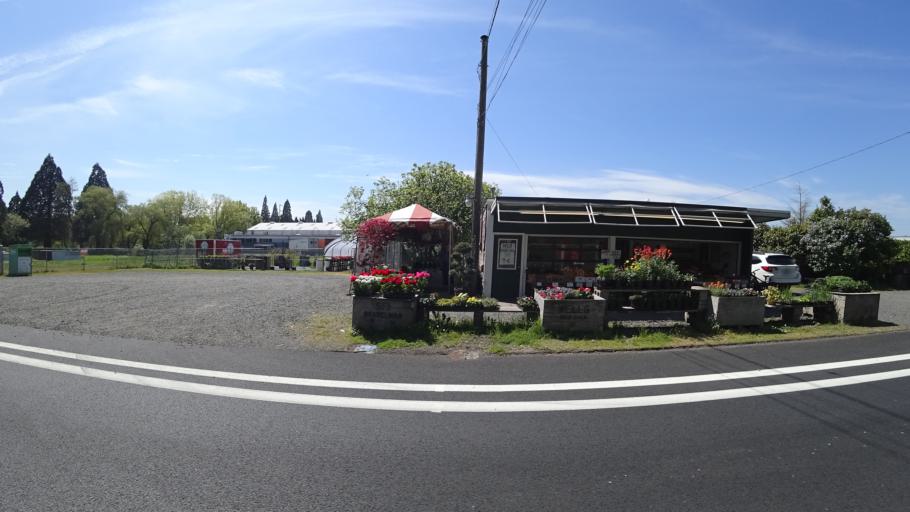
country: US
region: Oregon
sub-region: Clackamas County
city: Milwaukie
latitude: 45.4826
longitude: -122.6375
